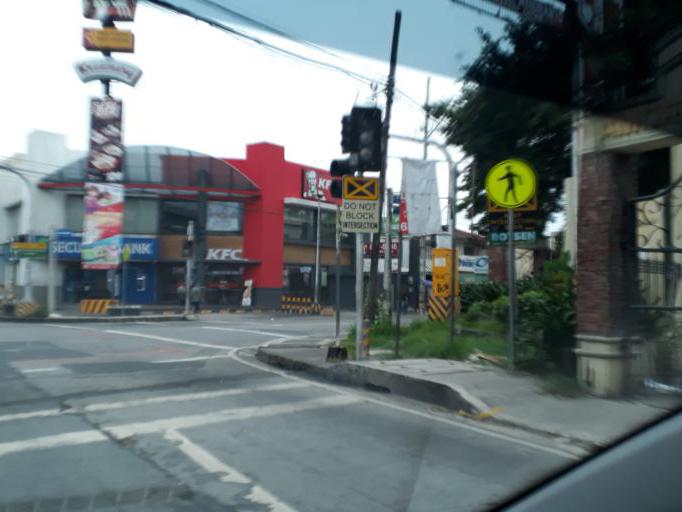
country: PH
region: Calabarzon
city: Del Monte
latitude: 14.6303
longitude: 120.9959
